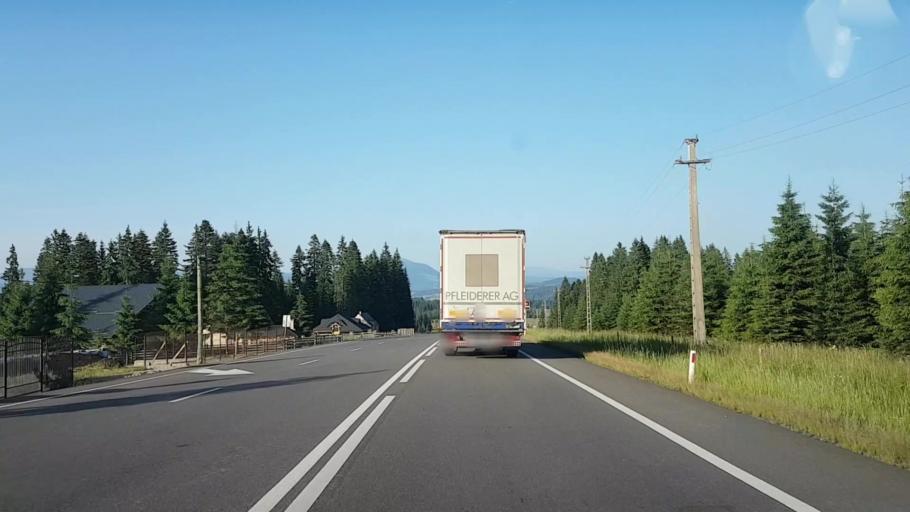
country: RO
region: Suceava
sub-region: Comuna Poiana Stampei
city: Poiana Stampei
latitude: 47.2959
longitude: 25.0856
